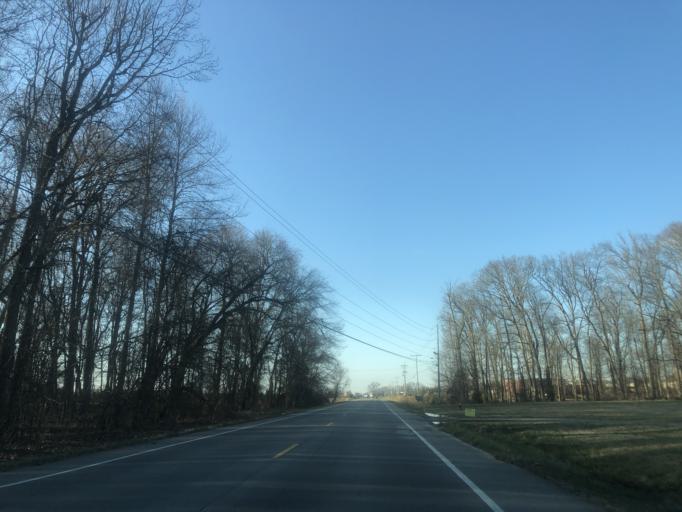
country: US
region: Tennessee
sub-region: Sumner County
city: Portland
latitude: 36.6269
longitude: -86.5585
